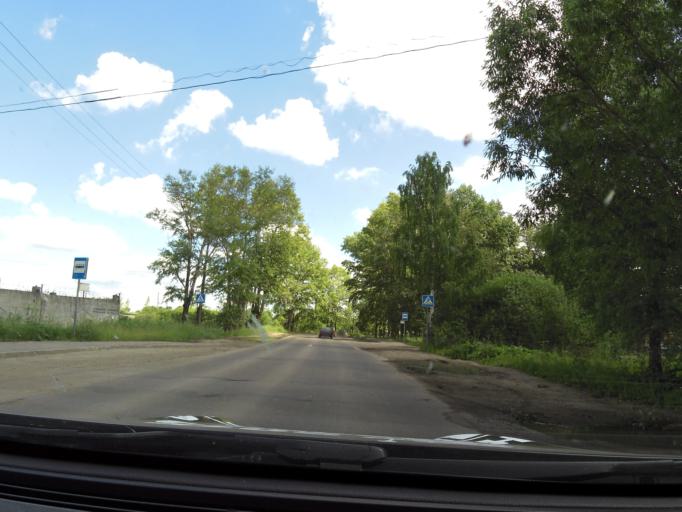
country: RU
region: Vologda
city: Vologda
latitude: 59.2377
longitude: 39.8176
